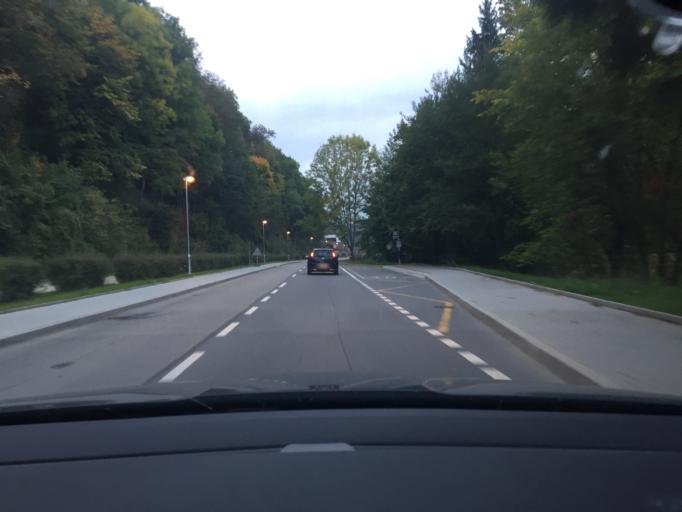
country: CZ
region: Jihocesky
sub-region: Okres Ceske Budejovice
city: Hluboka nad Vltavou
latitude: 49.0507
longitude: 14.4440
